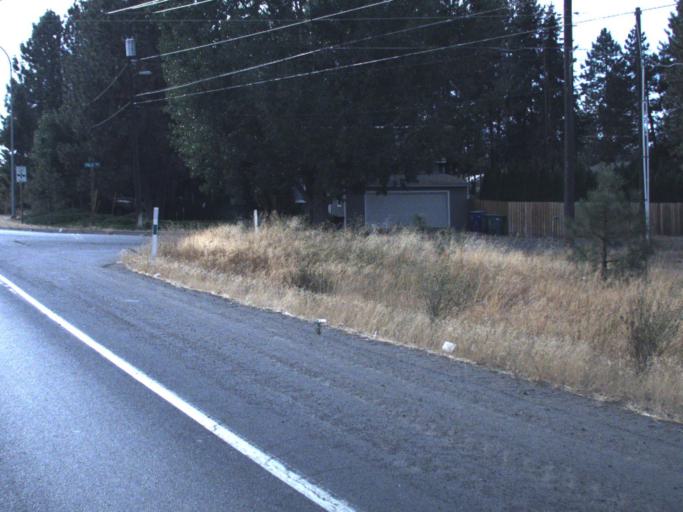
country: US
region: Washington
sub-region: Spokane County
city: Mead
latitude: 47.7874
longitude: -117.3466
